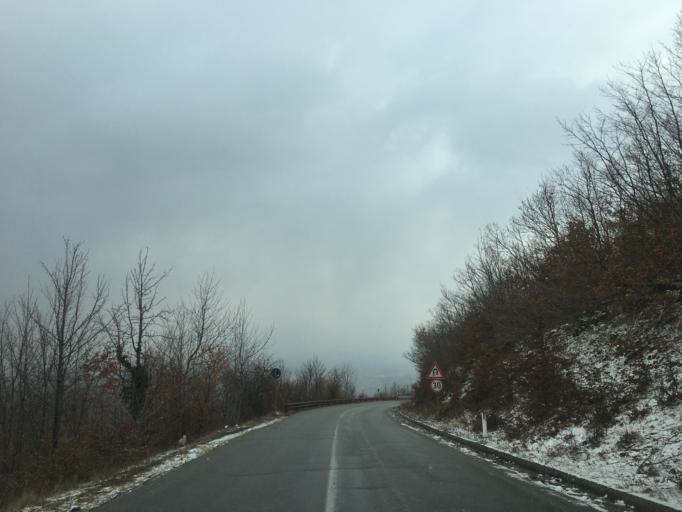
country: XK
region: Pec
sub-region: Komuna e Pejes
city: Dubova (Driloni)
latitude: 42.7509
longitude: 20.3025
